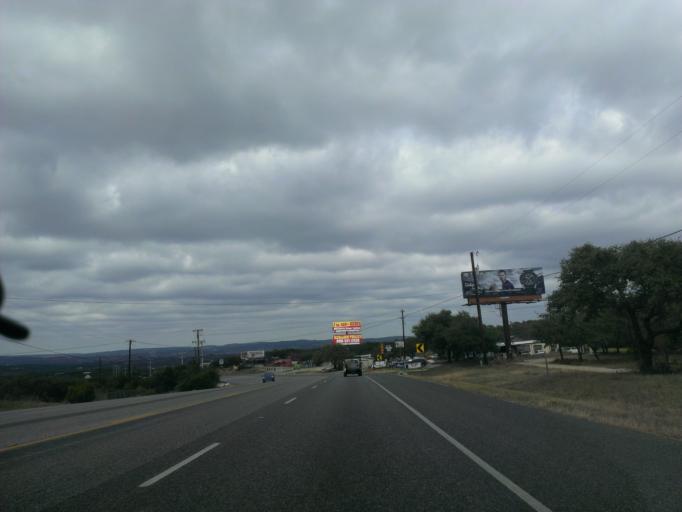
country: US
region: Texas
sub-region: Travis County
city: Briarcliff
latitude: 30.3675
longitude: -98.0721
